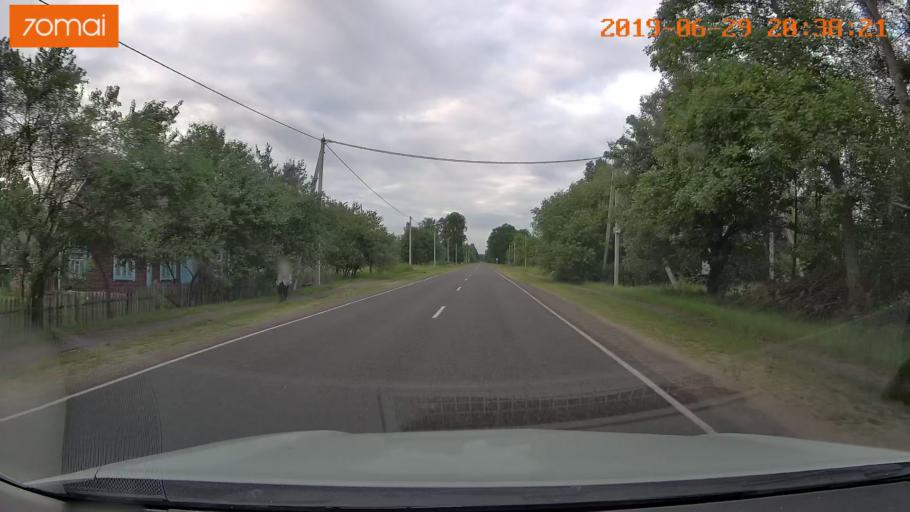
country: BY
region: Brest
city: Hantsavichy
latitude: 52.5490
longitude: 26.3648
